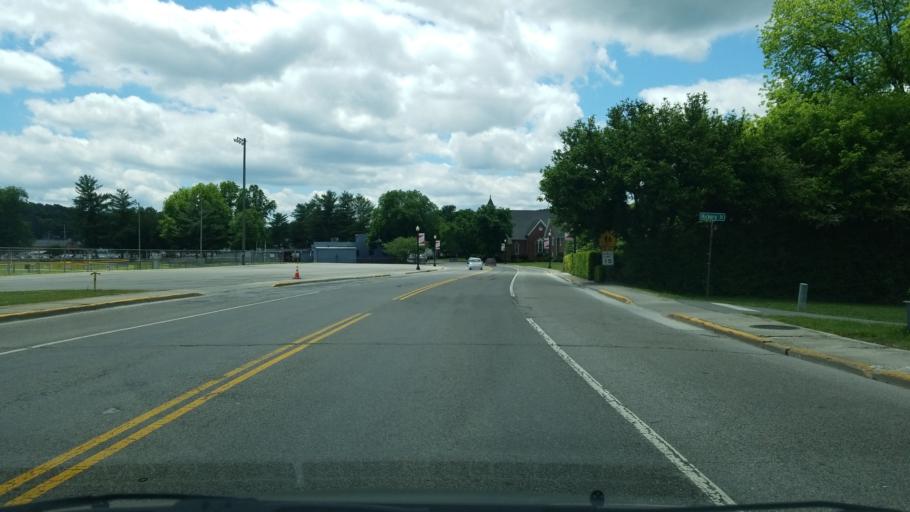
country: US
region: Tennessee
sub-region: Rhea County
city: Dayton
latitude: 35.4905
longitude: -85.0162
